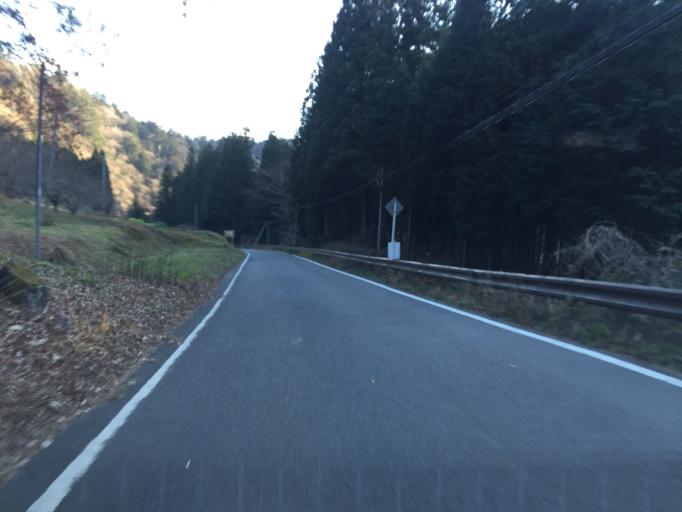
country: JP
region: Fukushima
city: Iwaki
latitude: 37.1690
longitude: 140.8256
